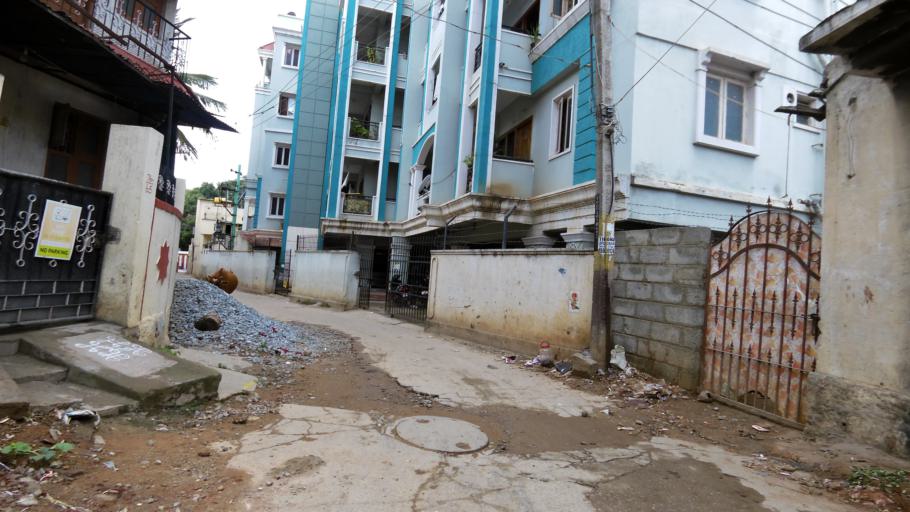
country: IN
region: Karnataka
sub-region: Bangalore Urban
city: Bangalore
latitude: 12.9955
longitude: 77.6288
